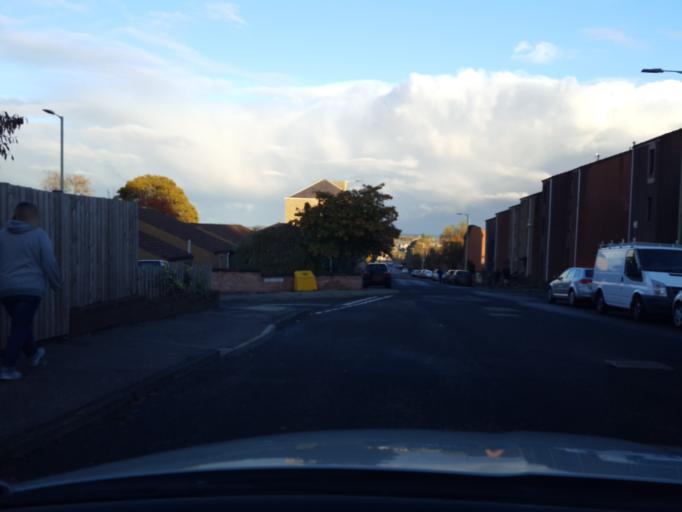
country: GB
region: Scotland
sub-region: Dundee City
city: Dundee
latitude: 56.4709
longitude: -2.9830
